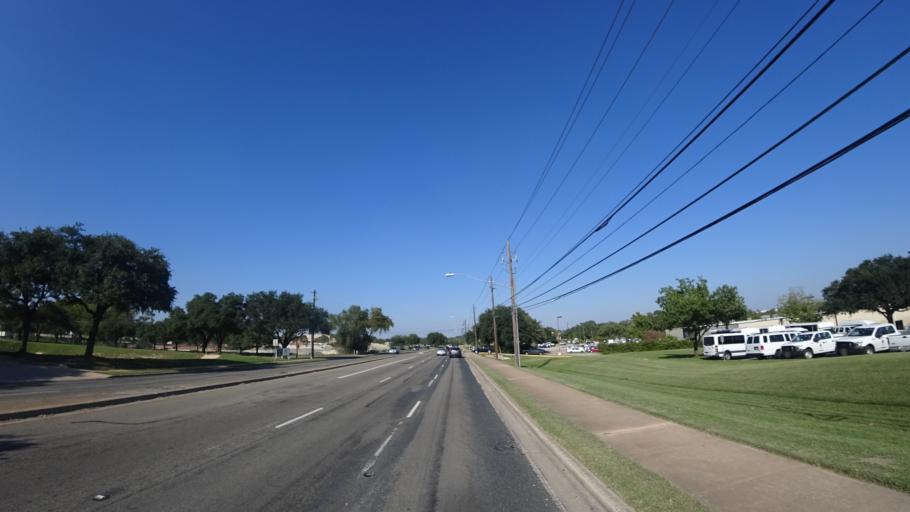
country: US
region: Texas
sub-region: Travis County
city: Austin
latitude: 30.3381
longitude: -97.6827
